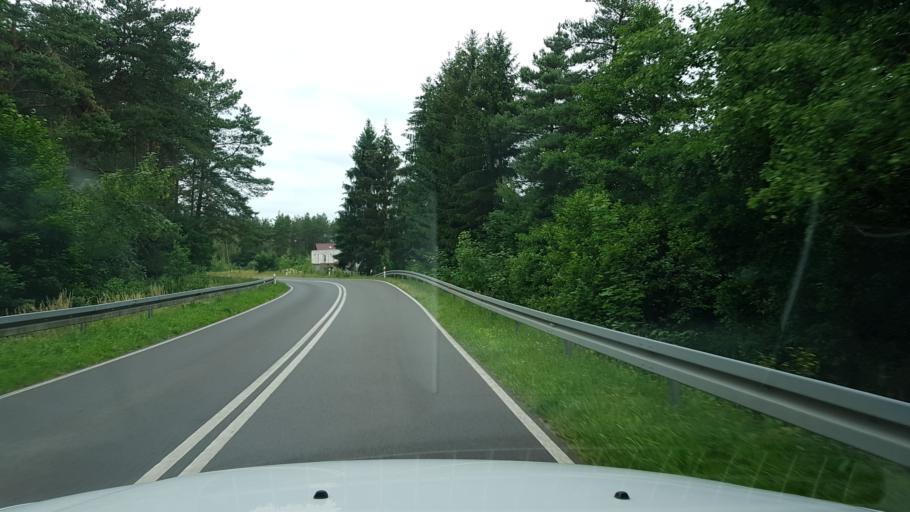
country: PL
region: West Pomeranian Voivodeship
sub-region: Powiat gryficki
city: Brojce
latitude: 53.9536
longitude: 15.3793
